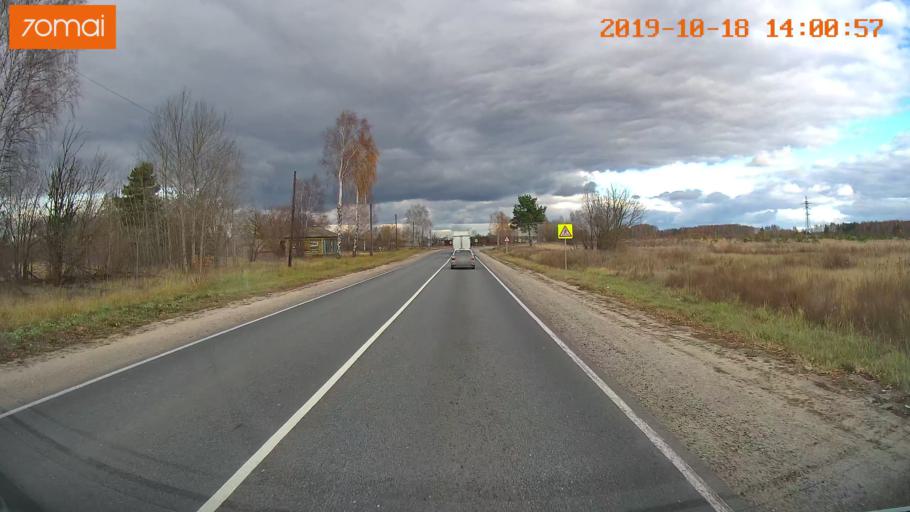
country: RU
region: Rjazan
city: Spas-Klepiki
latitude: 55.1045
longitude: 40.0823
